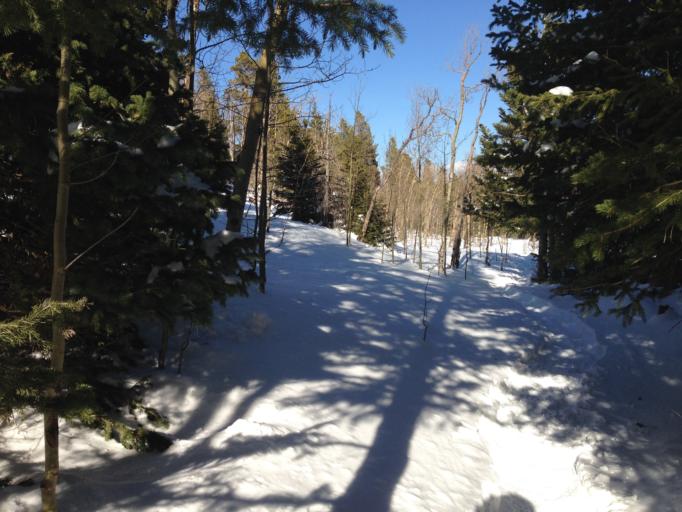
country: US
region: Colorado
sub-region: Boulder County
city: Nederland
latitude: 40.0941
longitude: -105.5043
